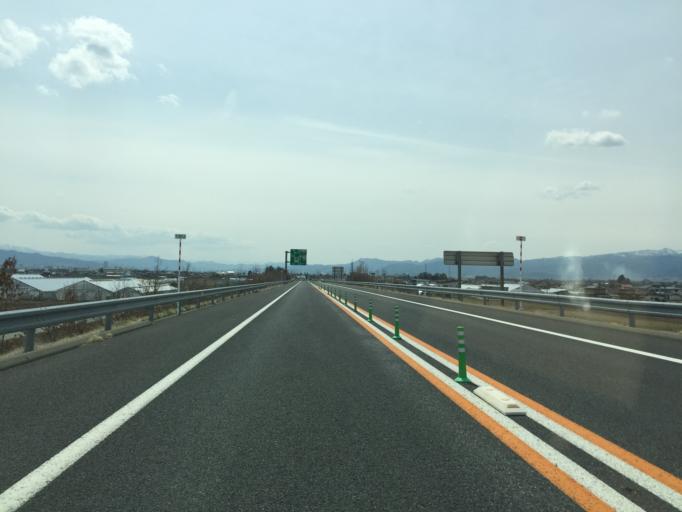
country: JP
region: Yamagata
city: Tendo
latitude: 38.3245
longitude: 140.3267
